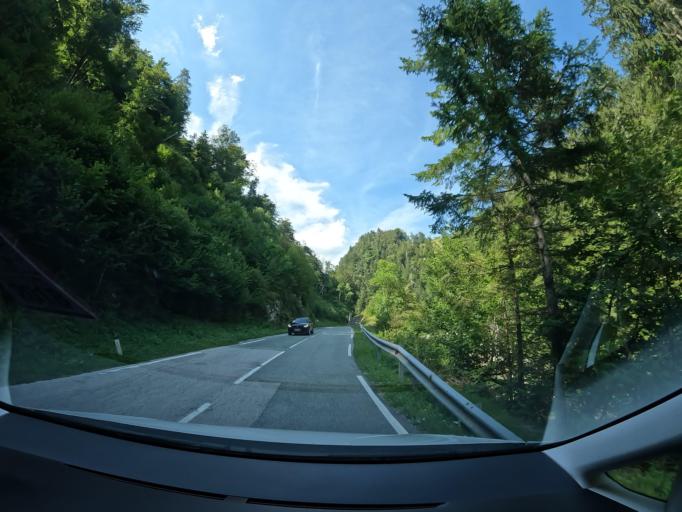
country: SI
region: Trzic
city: Trzic
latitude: 46.3862
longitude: 14.3683
